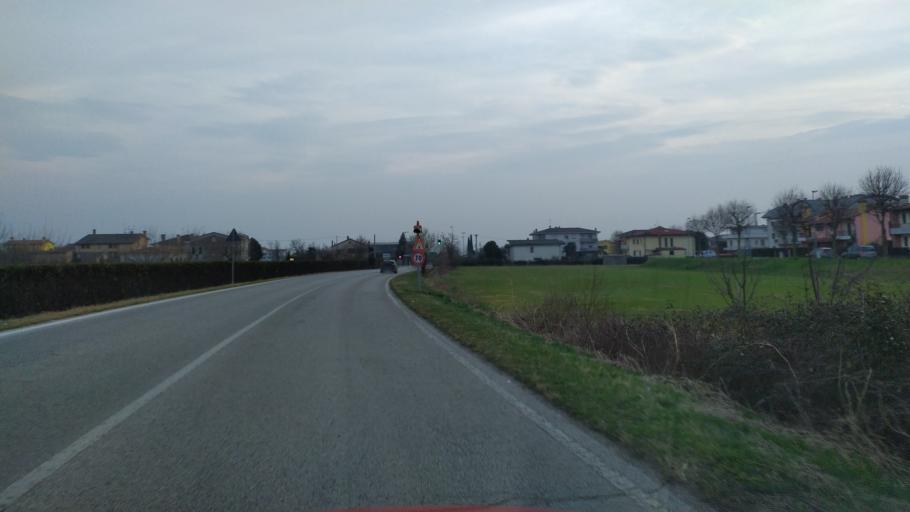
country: IT
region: Veneto
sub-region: Provincia di Vicenza
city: Dueville
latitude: 45.6433
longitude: 11.5575
